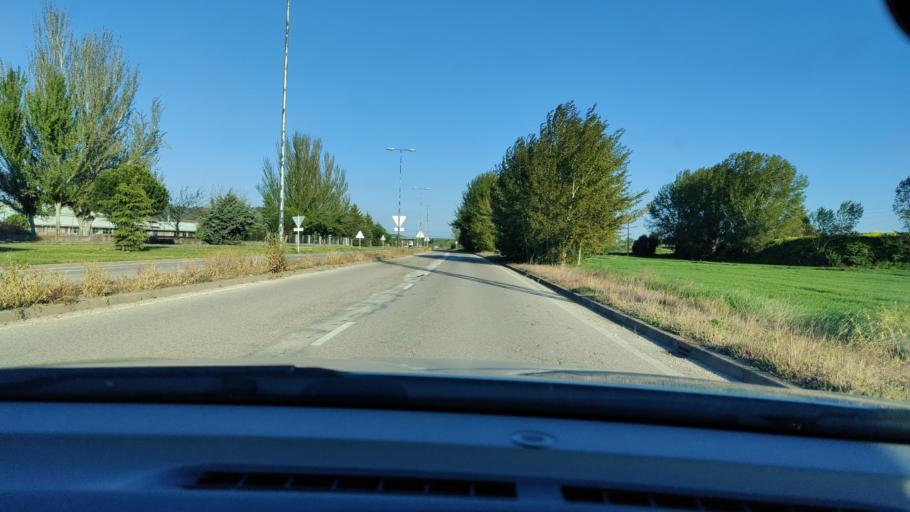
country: ES
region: Castille and Leon
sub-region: Provincia de Burgos
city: Villalbilla de Burgos
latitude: 42.3593
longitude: -3.7680
